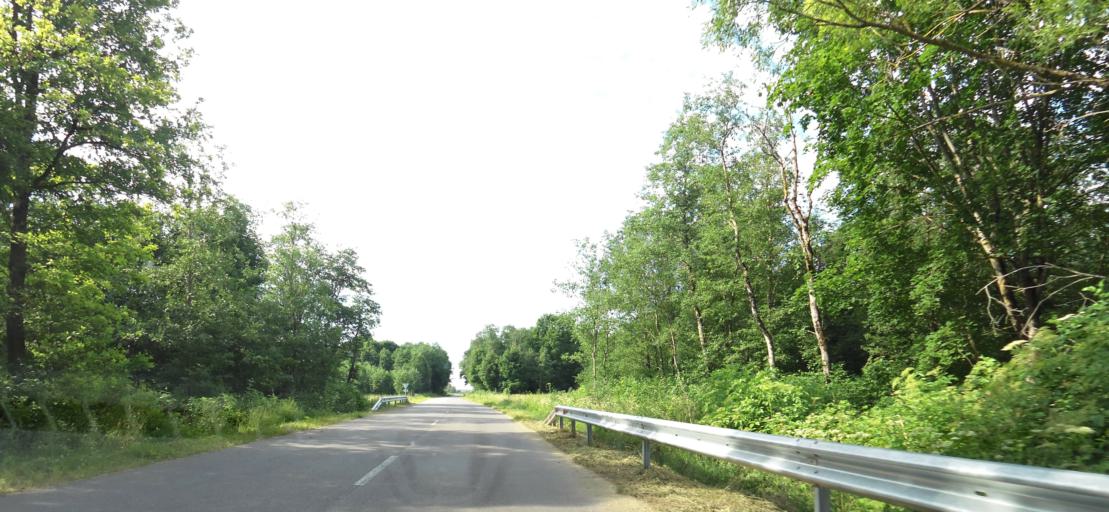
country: LT
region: Panevezys
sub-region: Birzai
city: Birzai
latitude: 56.2090
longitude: 24.6928
